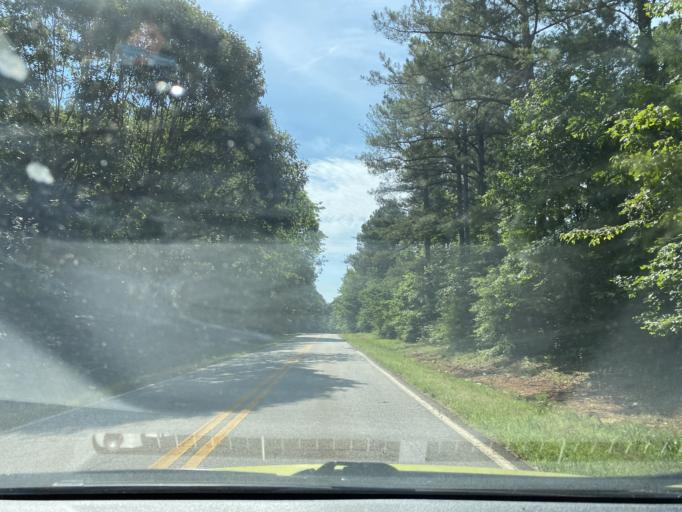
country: US
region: Georgia
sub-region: Meriwether County
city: Greenville
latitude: 33.1759
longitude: -84.6960
